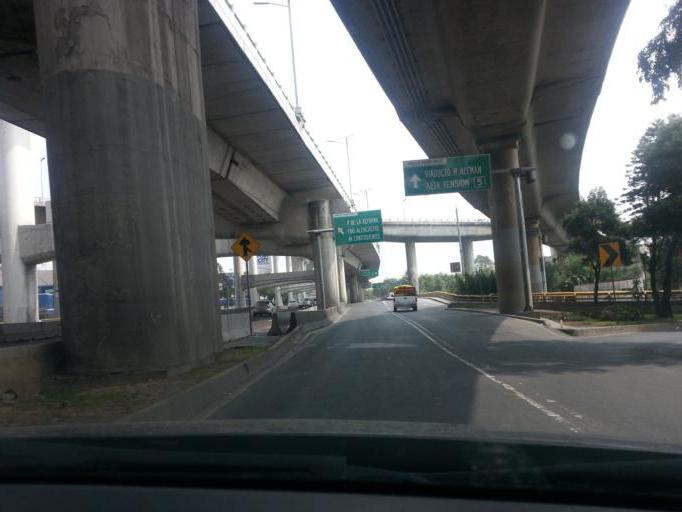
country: MX
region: Mexico City
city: Alvaro Obregon
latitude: 19.3840
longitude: -99.1912
